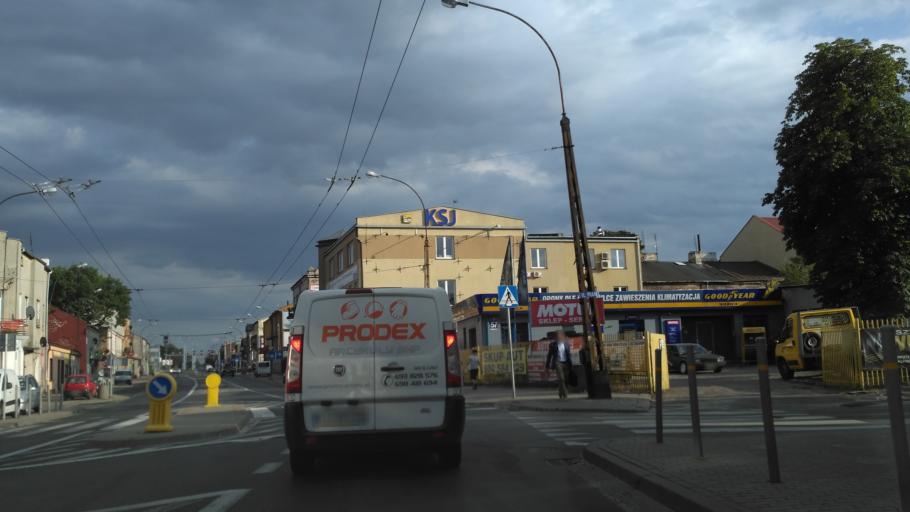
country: PL
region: Lublin Voivodeship
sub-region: Powiat lubelski
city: Lublin
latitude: 51.2263
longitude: 22.5729
